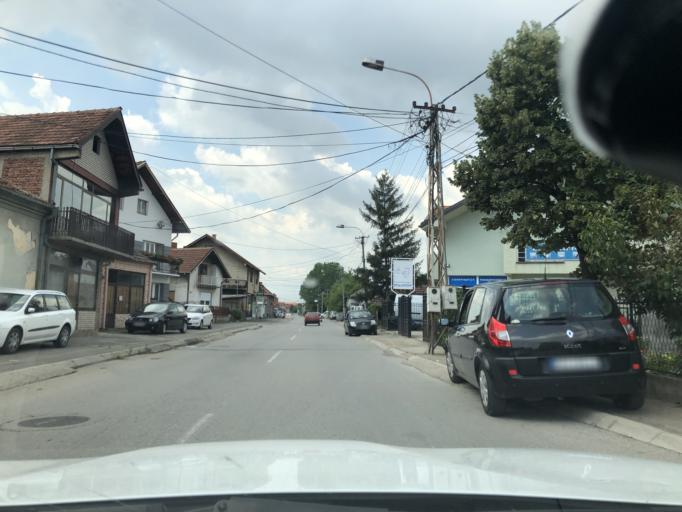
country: RS
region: Central Serbia
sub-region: Jablanicki Okrug
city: Leskovac
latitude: 42.9939
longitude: 21.9337
